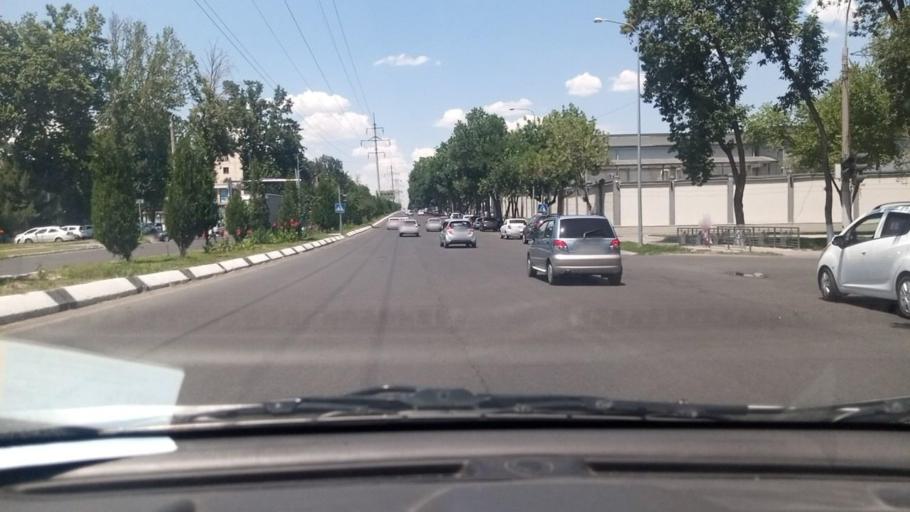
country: UZ
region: Toshkent Shahri
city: Tashkent
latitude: 41.2864
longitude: 69.1946
